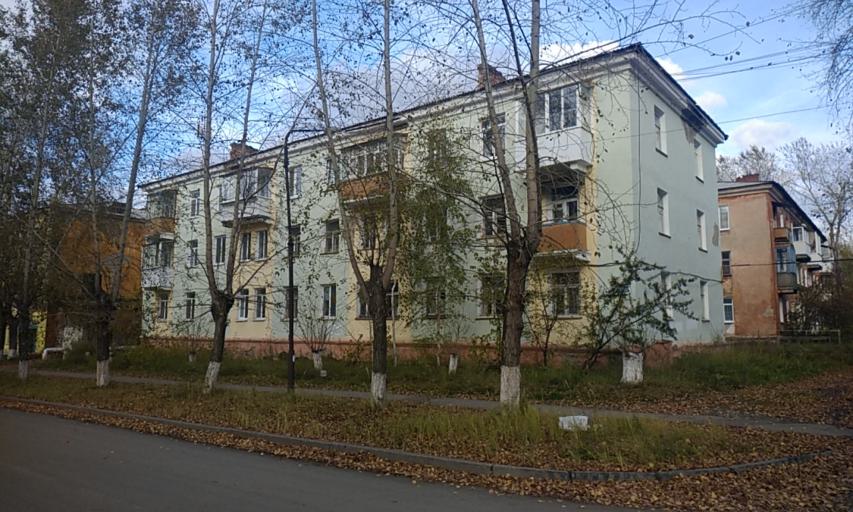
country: RU
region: Sverdlovsk
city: Krasnoural'sk
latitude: 58.3546
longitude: 60.0560
